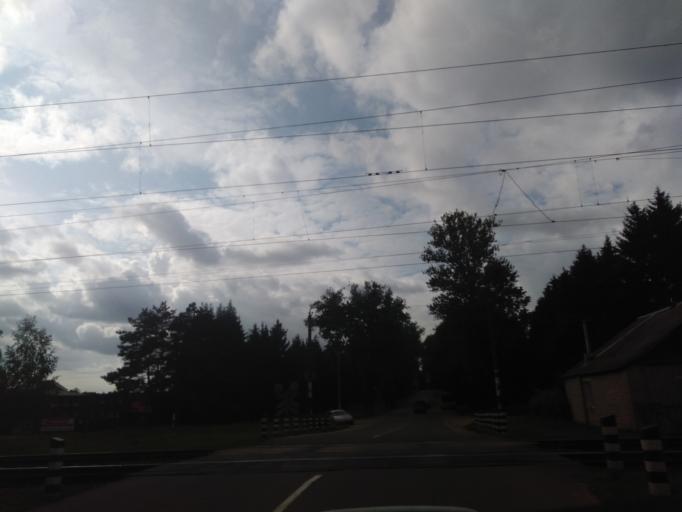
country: BY
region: Minsk
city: Korolev Stan
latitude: 53.9805
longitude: 27.8374
